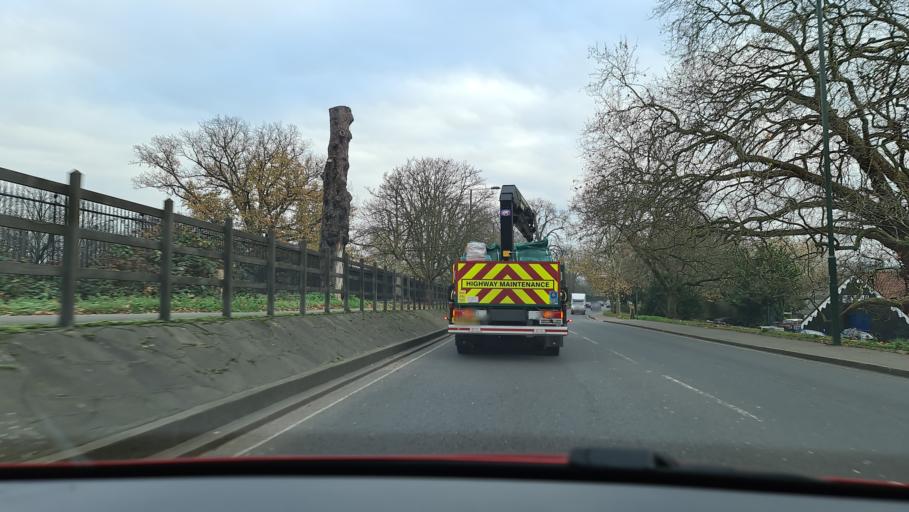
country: GB
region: England
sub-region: Greater London
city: Hampton
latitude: 51.4111
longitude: -0.3541
